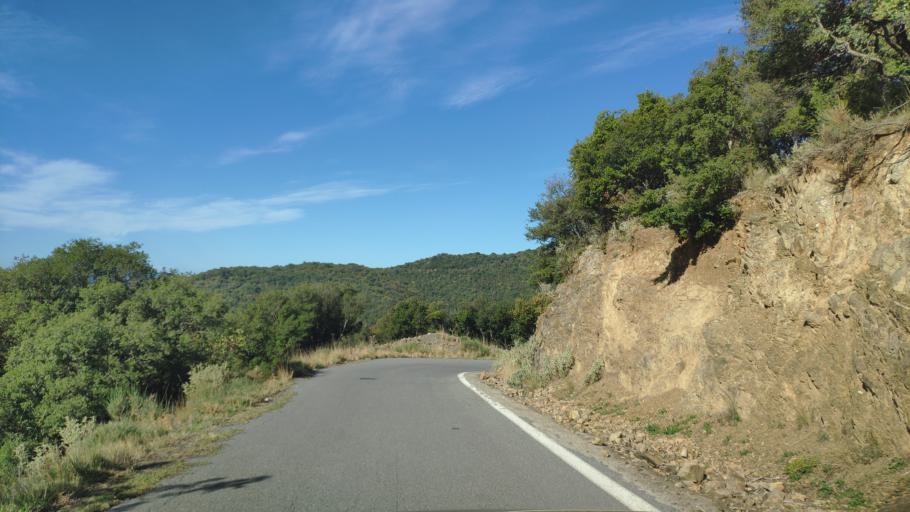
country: GR
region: Peloponnese
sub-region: Nomos Arkadias
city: Dimitsana
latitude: 37.5517
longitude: 22.0568
